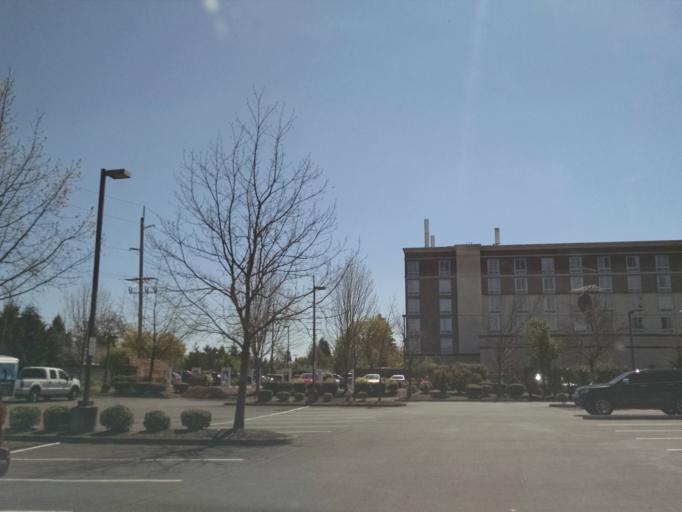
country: US
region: Oregon
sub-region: Lane County
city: Springfield
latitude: 44.0832
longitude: -123.0377
